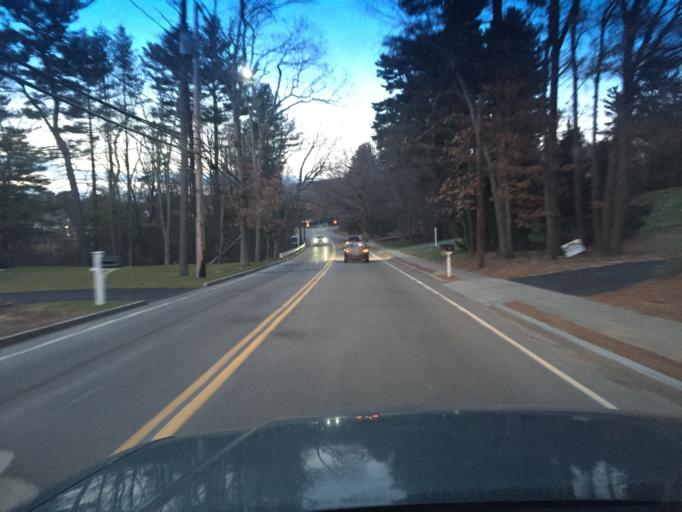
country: US
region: Massachusetts
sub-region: Norfolk County
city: Westwood
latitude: 42.2070
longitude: -71.2224
